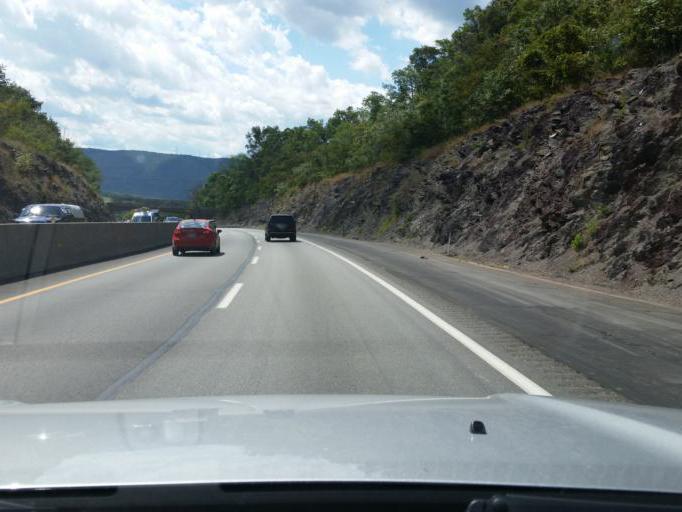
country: US
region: Pennsylvania
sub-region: Bedford County
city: Earlston
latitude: 40.0011
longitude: -78.3478
